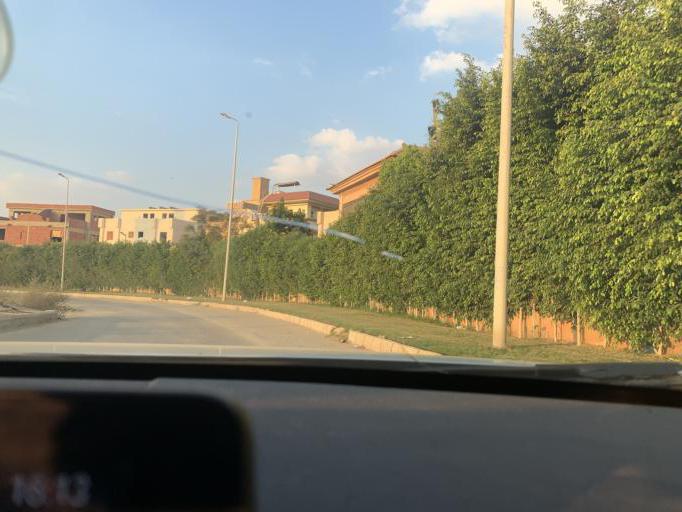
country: EG
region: Muhafazat al Qalyubiyah
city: Al Khankah
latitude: 30.0223
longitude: 31.4814
